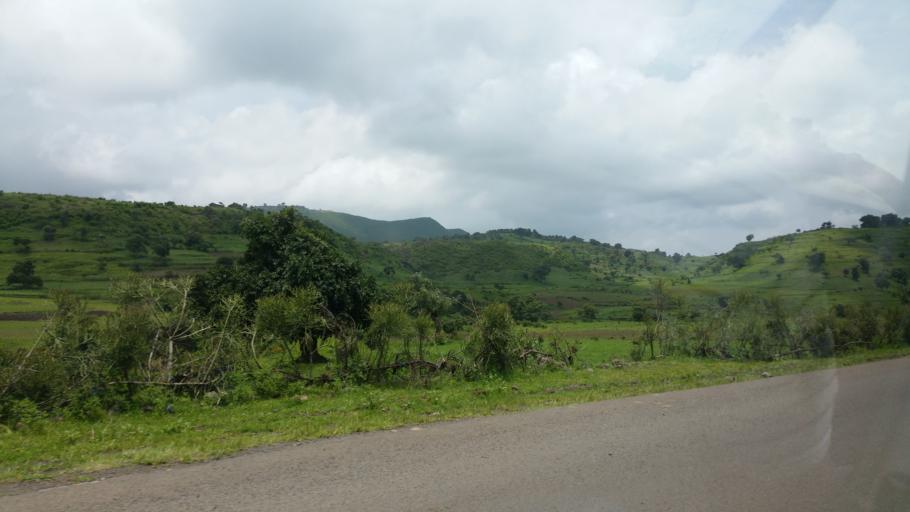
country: ET
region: Amhara
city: Adis Zemen
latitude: 12.1729
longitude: 37.7010
